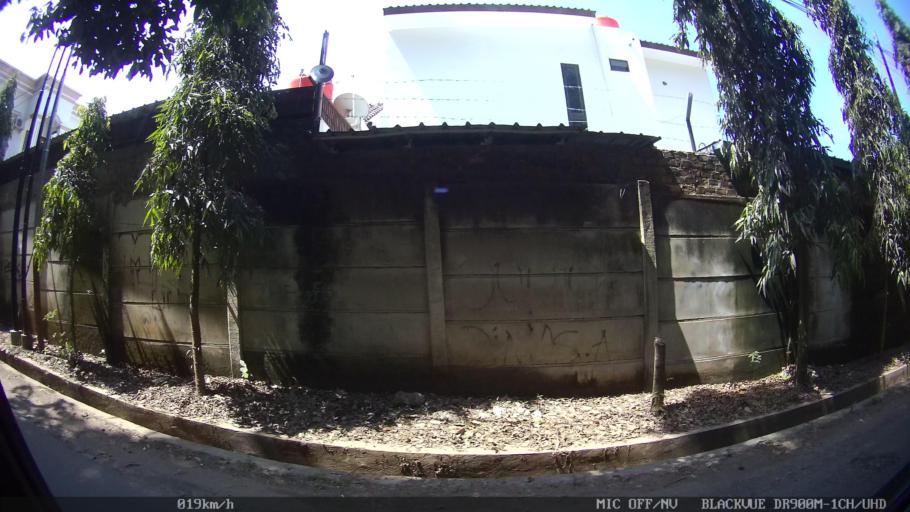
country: ID
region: Lampung
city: Kedaton
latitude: -5.3692
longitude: 105.2568
